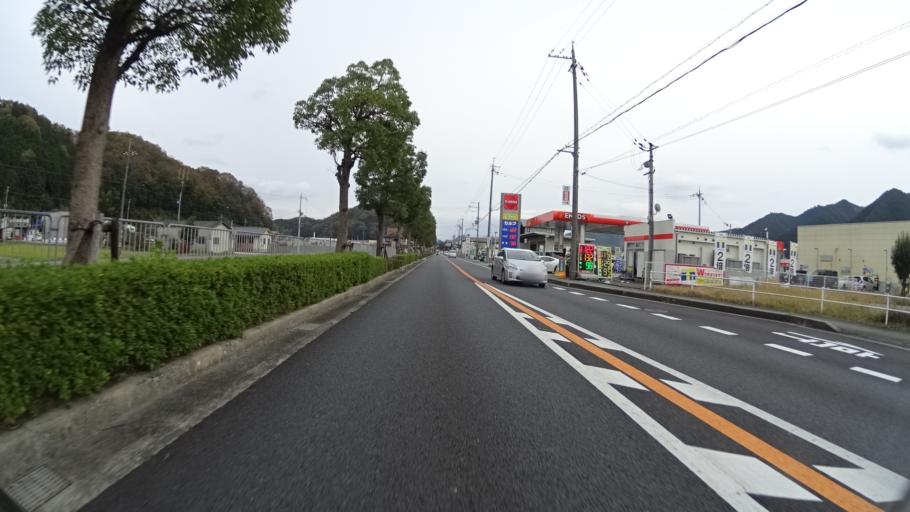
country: JP
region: Hyogo
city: Sasayama
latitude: 35.0644
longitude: 135.1863
